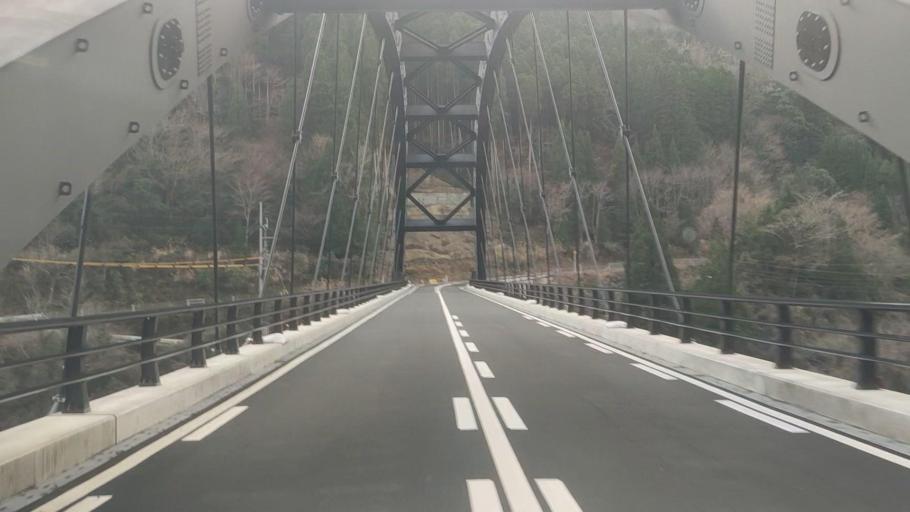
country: JP
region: Kumamoto
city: Hitoyoshi
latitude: 32.4116
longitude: 130.8403
